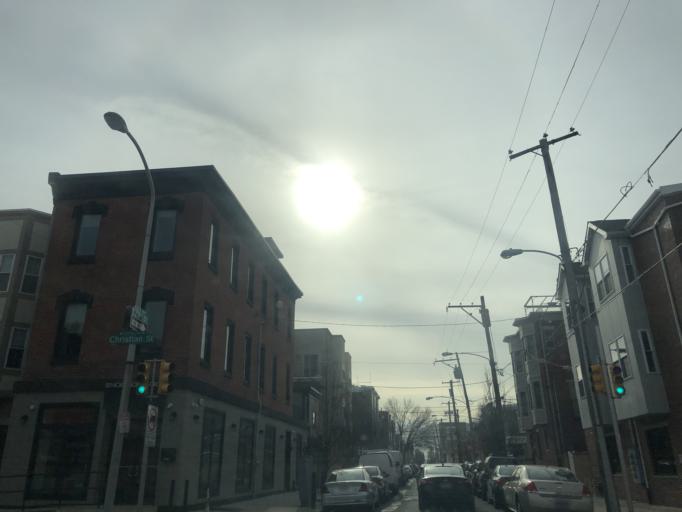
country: US
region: Pennsylvania
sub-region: Philadelphia County
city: Philadelphia
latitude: 39.9420
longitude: -75.1810
